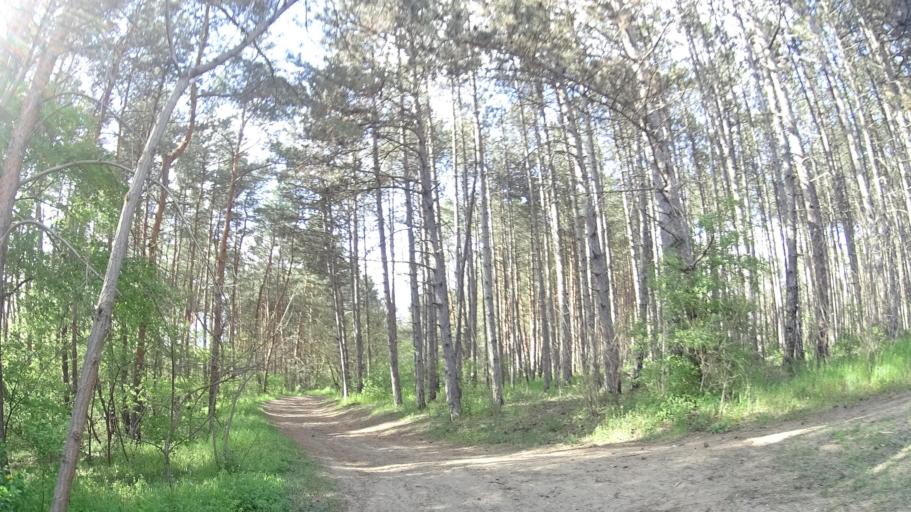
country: HU
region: Pest
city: Veresegyhaz
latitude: 47.6387
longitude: 19.2795
